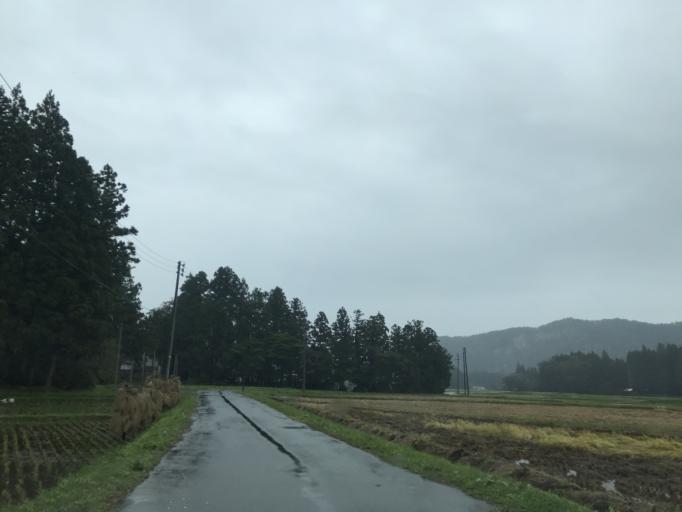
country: JP
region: Iwate
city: Ichinoseki
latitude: 38.9777
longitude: 140.9571
